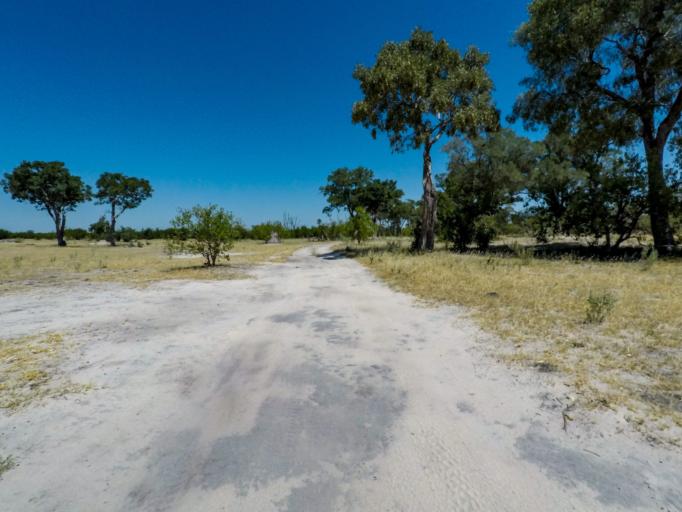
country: BW
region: North West
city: Maun
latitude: -19.4367
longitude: 23.5646
